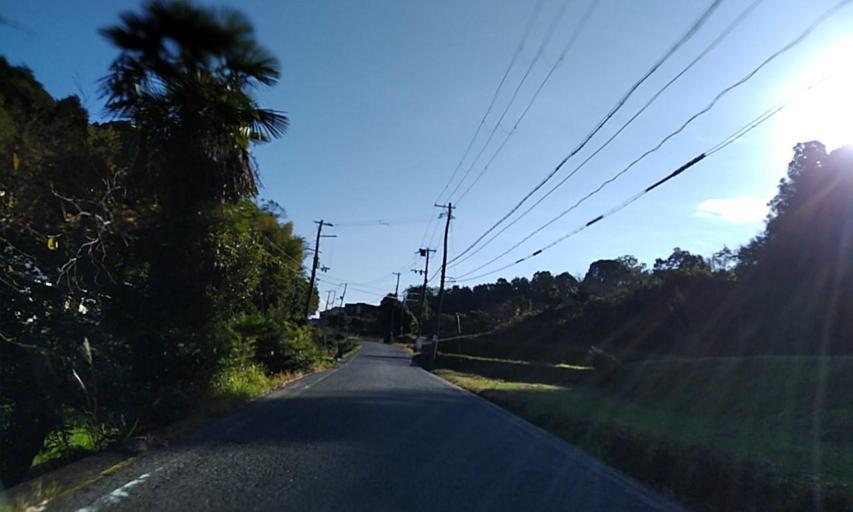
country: JP
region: Wakayama
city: Iwade
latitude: 34.1555
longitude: 135.2991
